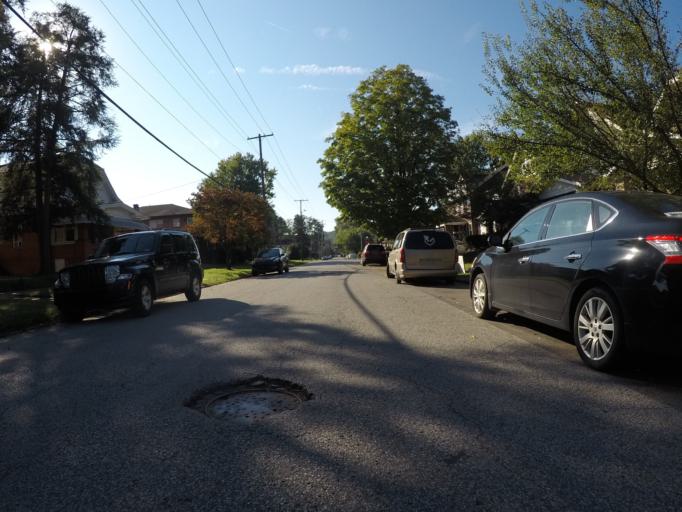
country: US
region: West Virginia
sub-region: Cabell County
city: Huntington
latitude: 38.4139
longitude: -82.4365
